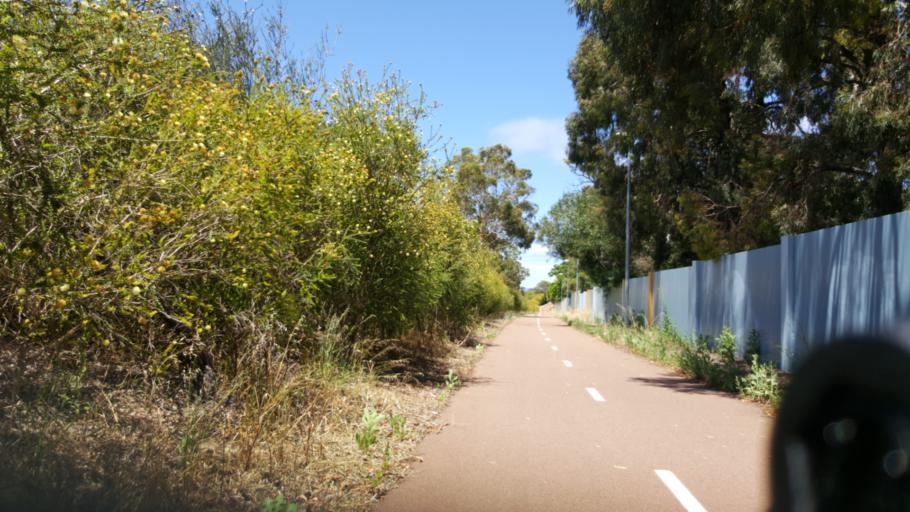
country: AU
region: Western Australia
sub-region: Stirling
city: Westminster
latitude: -31.8687
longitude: 115.8797
